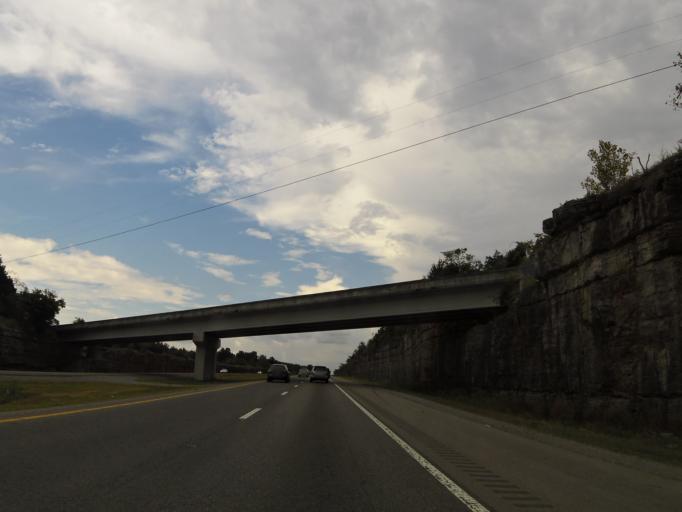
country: US
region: Tennessee
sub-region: Rutherford County
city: Smyrna
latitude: 35.9515
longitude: -86.4416
